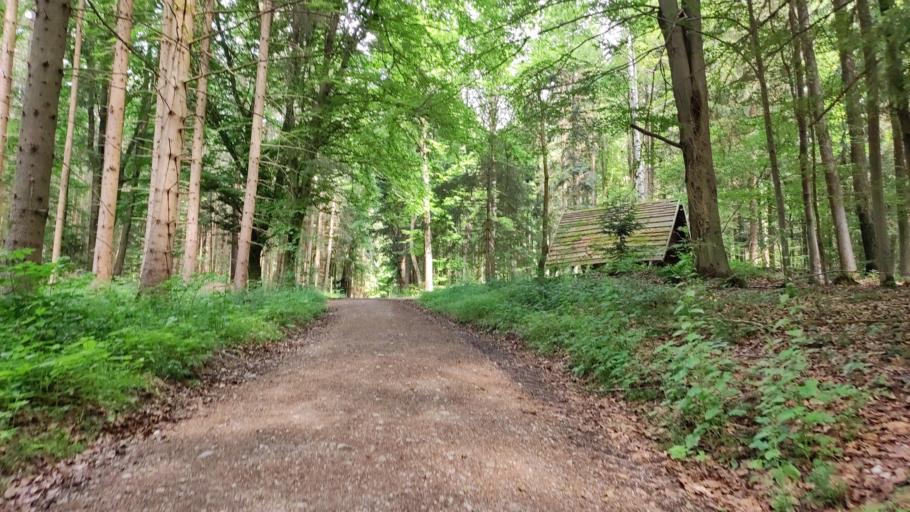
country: DE
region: Bavaria
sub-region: Swabia
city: Adelsried
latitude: 48.4078
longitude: 10.7001
